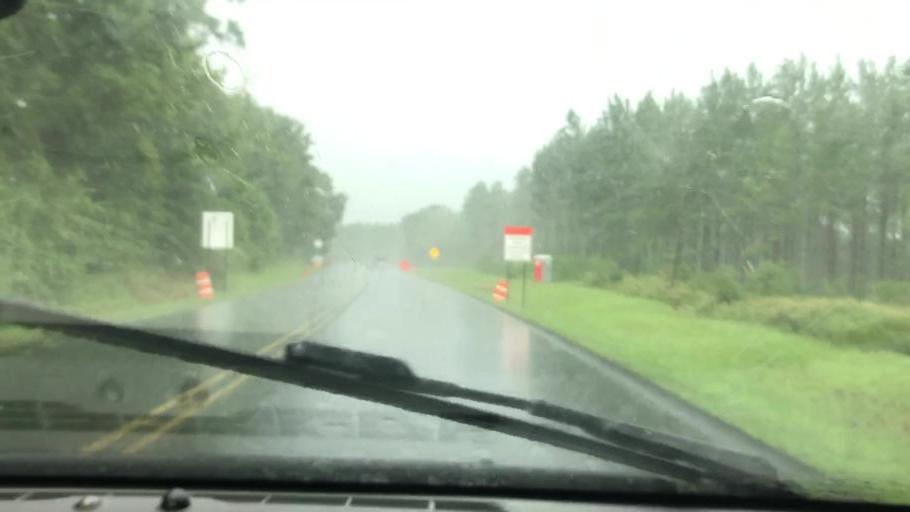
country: US
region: Georgia
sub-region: Clay County
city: Fort Gaines
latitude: 31.5533
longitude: -85.0194
